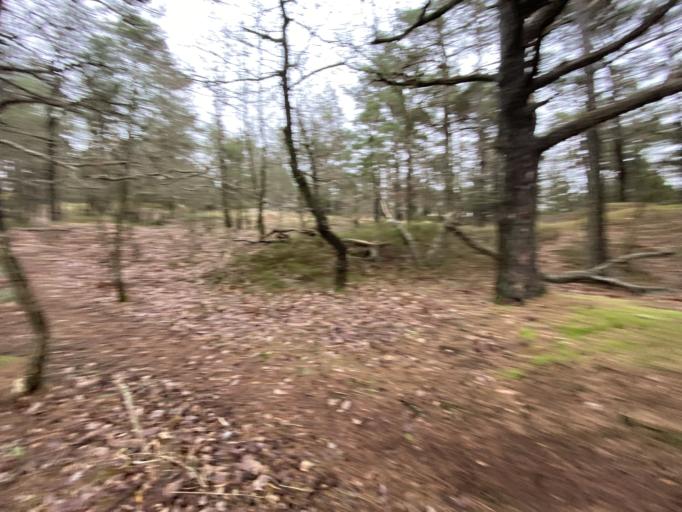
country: SE
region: Vaestra Goetaland
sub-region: Molndal
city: Moelndal
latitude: 57.7090
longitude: 12.0330
